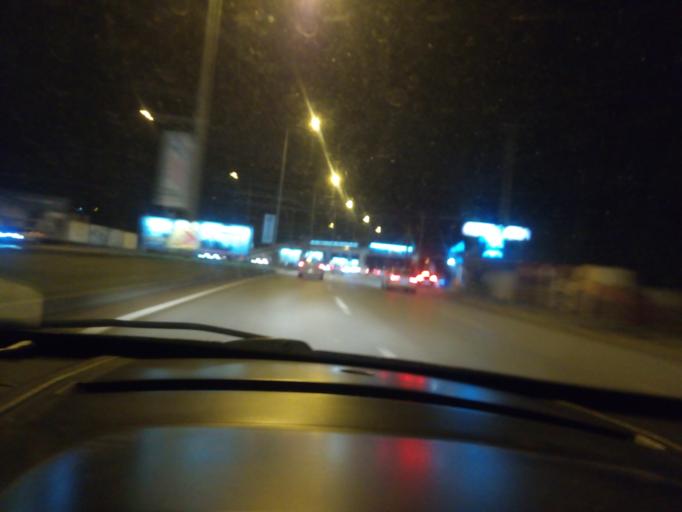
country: TR
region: Bursa
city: Niluefer
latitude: 40.2830
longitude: 28.9343
